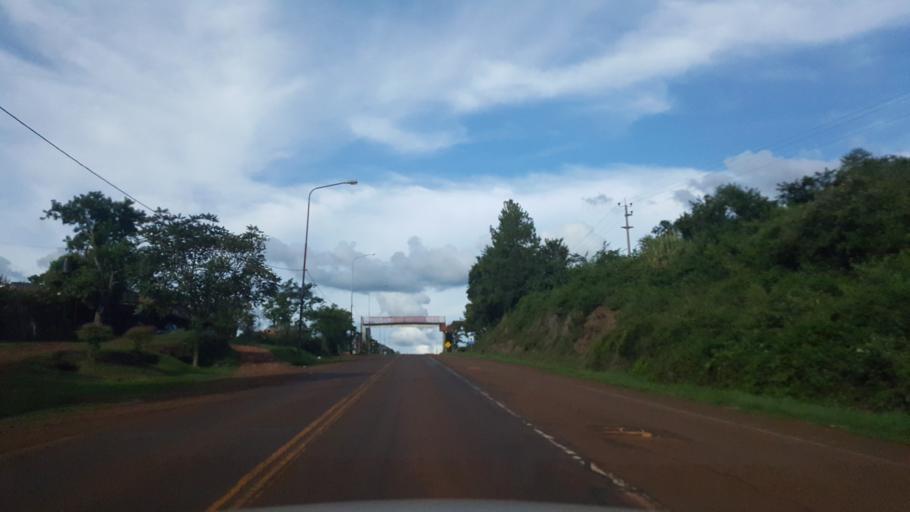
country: AR
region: Misiones
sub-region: Departamento de San Ignacio
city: San Ignacio
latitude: -27.2627
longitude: -55.5335
